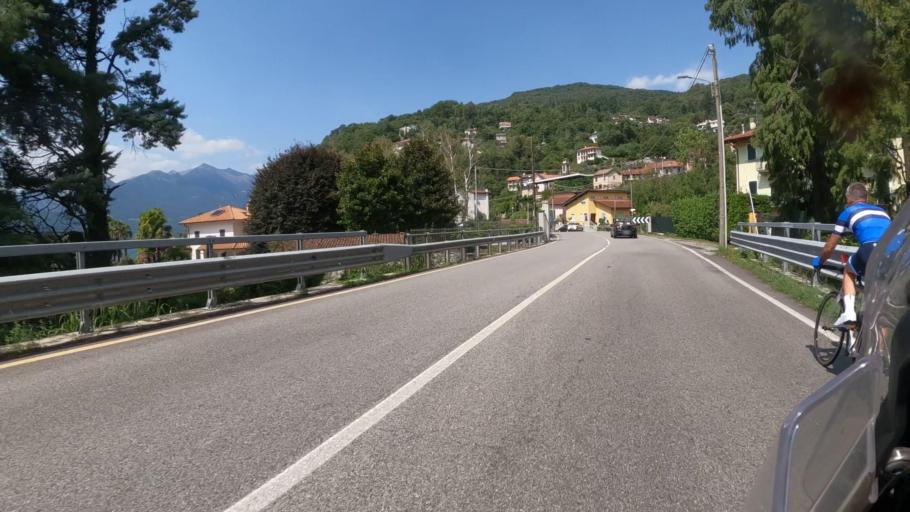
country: IT
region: Lombardy
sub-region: Provincia di Varese
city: Agra
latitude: 46.0233
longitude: 8.7519
